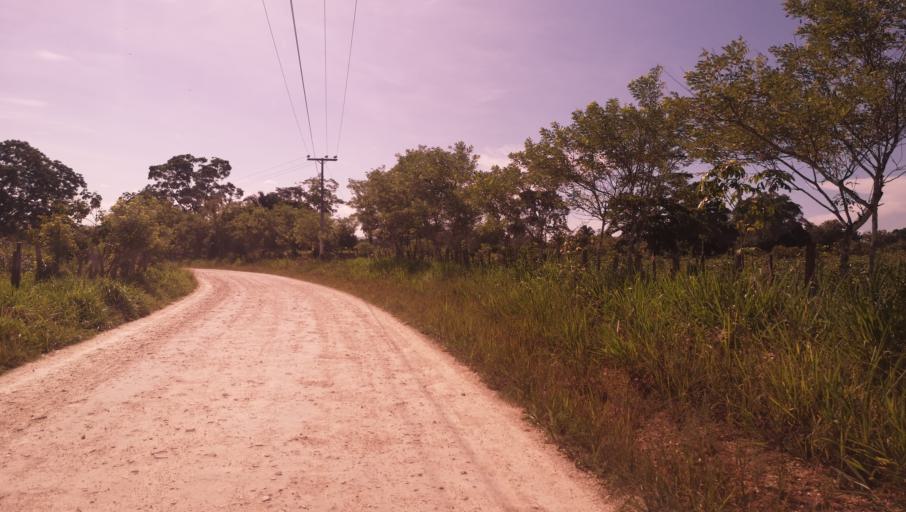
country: GT
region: Peten
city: Dolores
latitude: 16.7147
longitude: -89.3664
